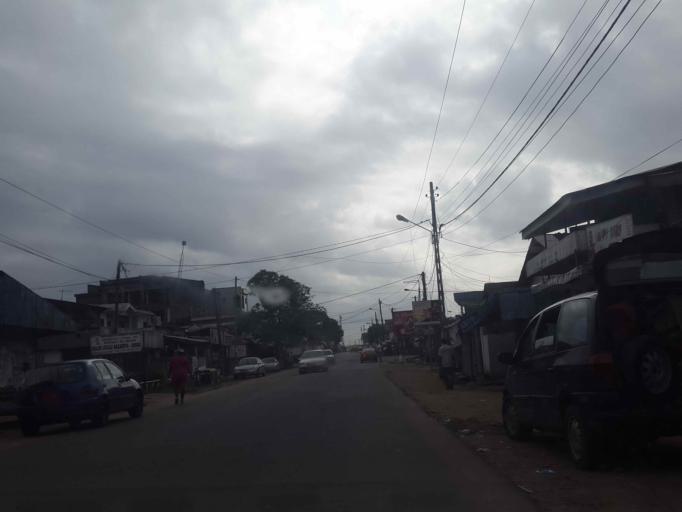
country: CM
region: Littoral
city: Douala
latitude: 4.0683
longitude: 9.7113
